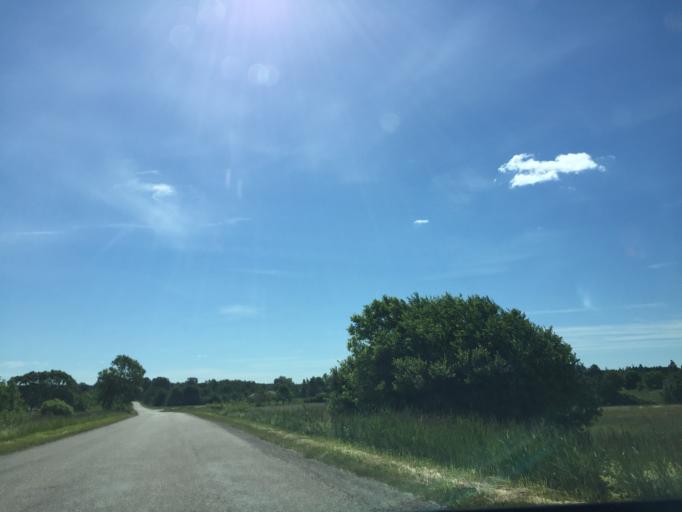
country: LV
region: Dundaga
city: Dundaga
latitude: 57.3580
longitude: 22.0477
